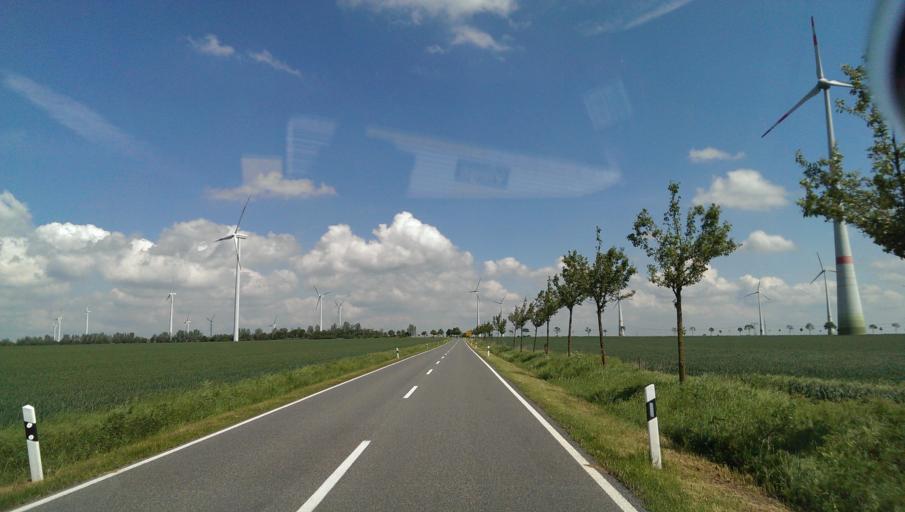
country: DE
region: Saxony-Anhalt
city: Atzendorf
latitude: 51.9552
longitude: 11.5992
